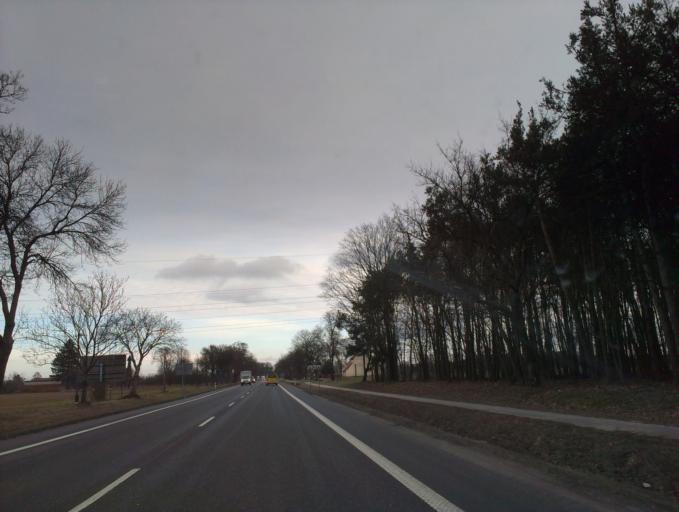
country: PL
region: Masovian Voivodeship
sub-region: Powiat sierpecki
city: Sierpc
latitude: 52.8672
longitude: 19.6536
